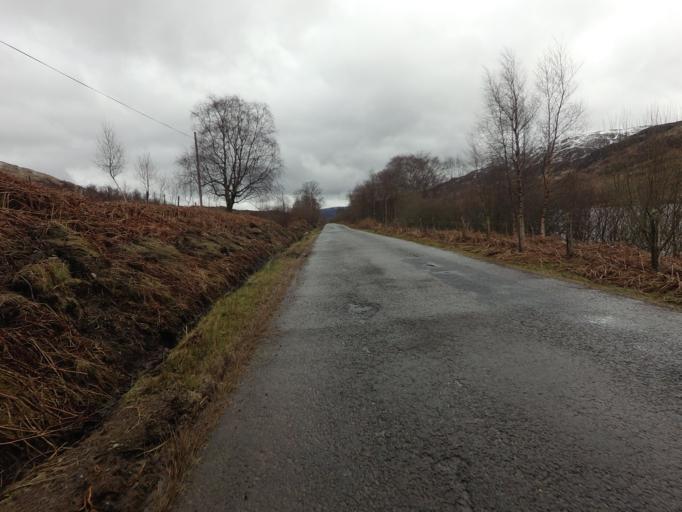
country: GB
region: Scotland
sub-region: Argyll and Bute
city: Garelochhead
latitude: 56.2484
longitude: -4.6402
